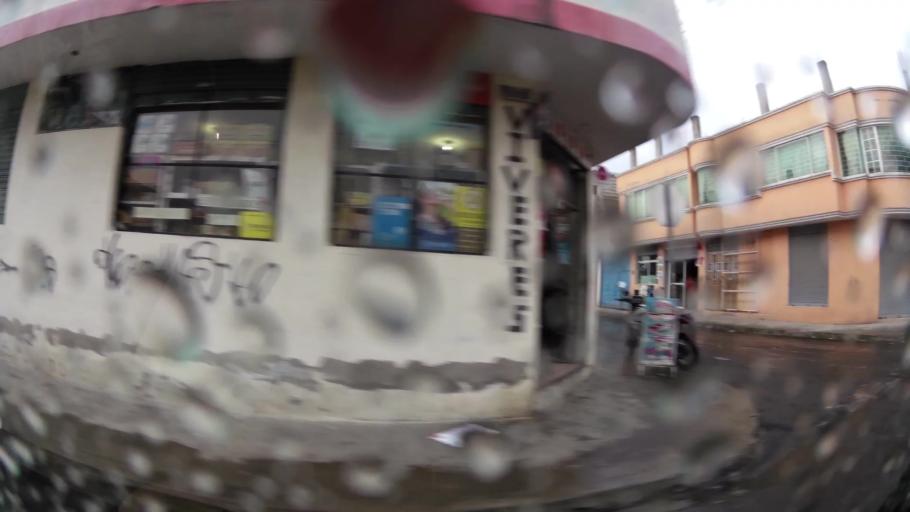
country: EC
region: Pichincha
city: Quito
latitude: -0.3109
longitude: -78.5503
